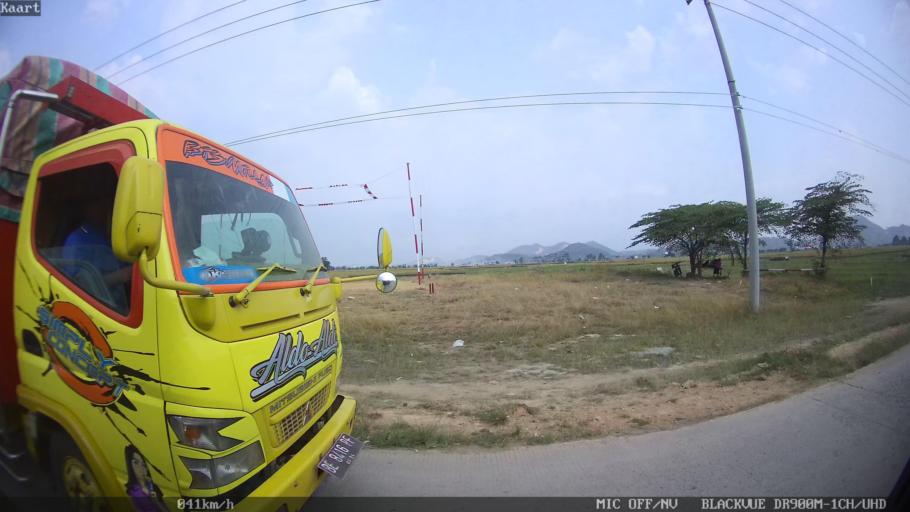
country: ID
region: Lampung
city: Pringsewu
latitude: -5.3605
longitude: 105.0078
